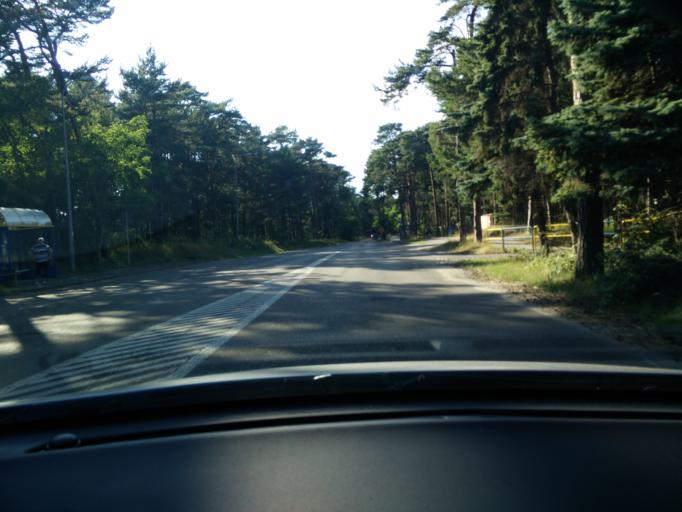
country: PL
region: Pomeranian Voivodeship
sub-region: Powiat pucki
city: Jastarnia
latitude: 54.6735
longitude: 18.7293
